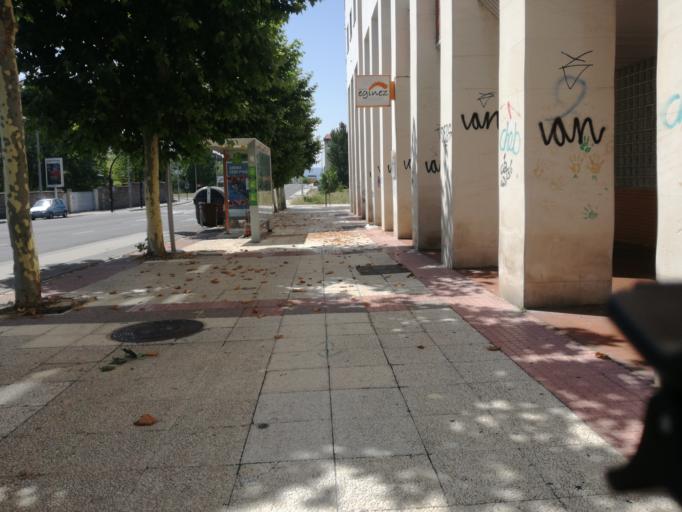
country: ES
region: Basque Country
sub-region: Provincia de Alava
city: Gasteiz / Vitoria
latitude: 42.8520
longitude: -2.6911
